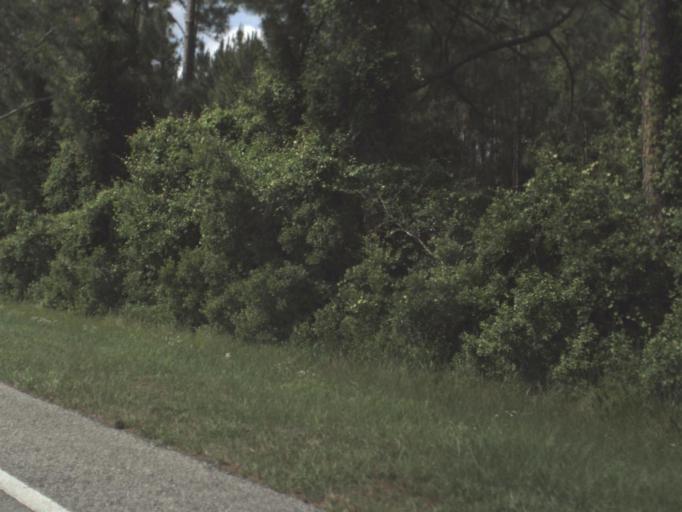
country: US
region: Florida
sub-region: Saint Johns County
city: Butler Beach
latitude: 29.7008
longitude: -81.2981
